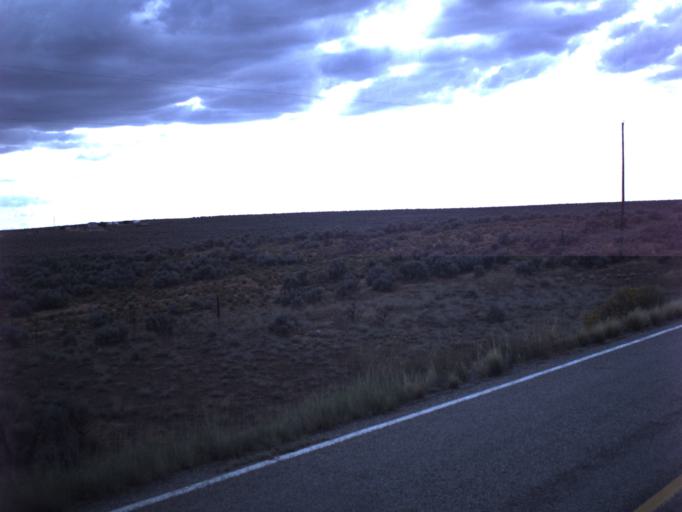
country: US
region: Utah
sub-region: San Juan County
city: Blanding
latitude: 37.4263
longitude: -109.3502
